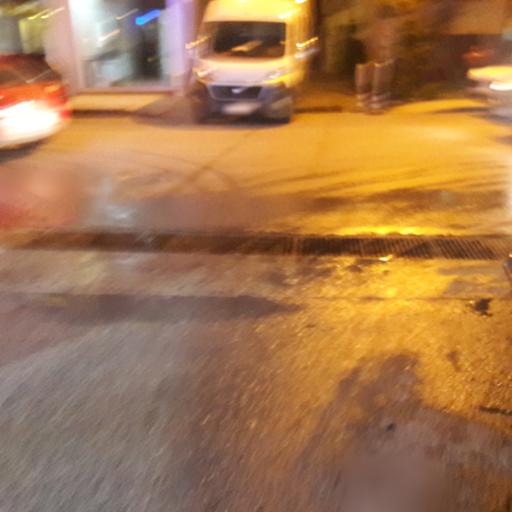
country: TR
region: Sinop
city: Sinop
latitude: 42.0247
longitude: 35.1487
